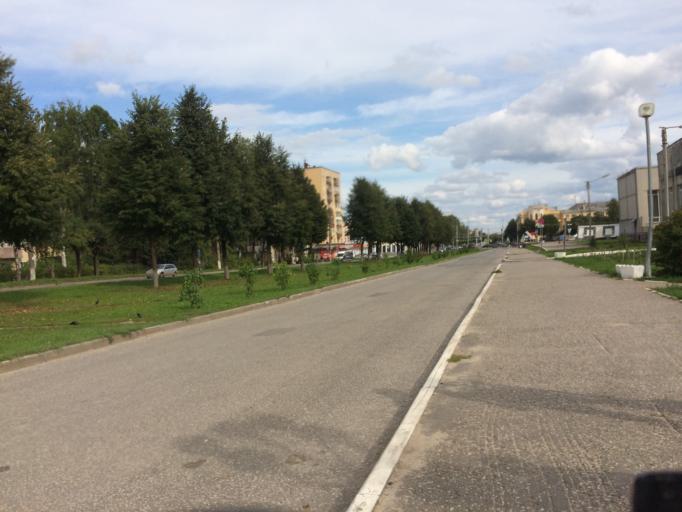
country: RU
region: Mariy-El
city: Yoshkar-Ola
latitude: 56.6409
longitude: 47.8676
